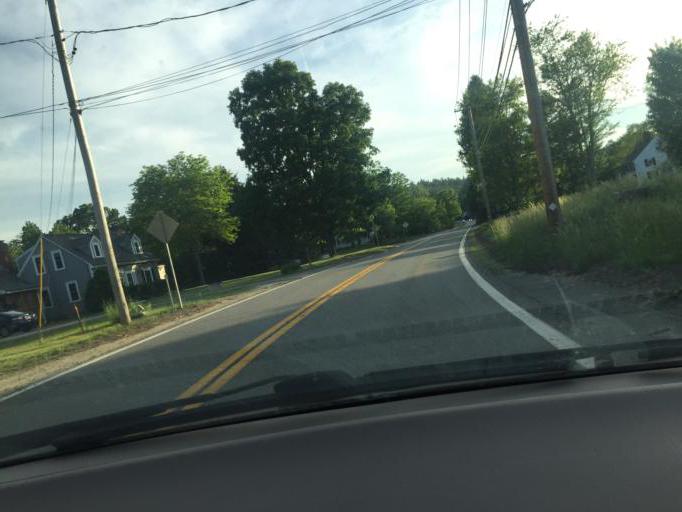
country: US
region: Massachusetts
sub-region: Middlesex County
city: Townsend
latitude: 42.6763
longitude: -71.7568
